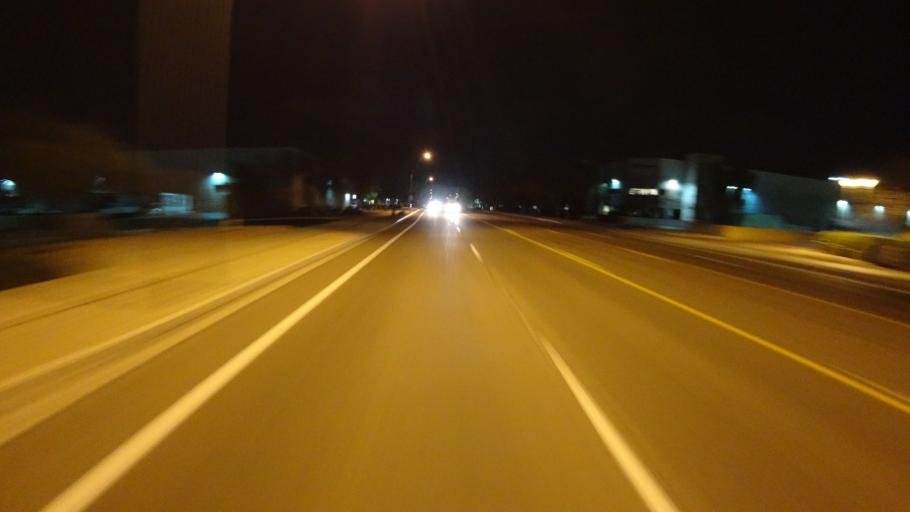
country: US
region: Arizona
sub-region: Maricopa County
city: Guadalupe
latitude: 33.3327
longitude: -111.9456
